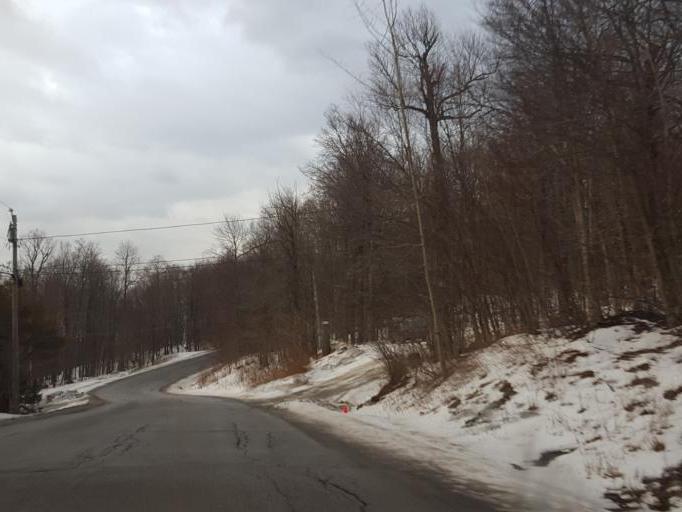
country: US
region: Vermont
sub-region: Rutland County
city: Rutland
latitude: 43.6291
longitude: -72.7719
